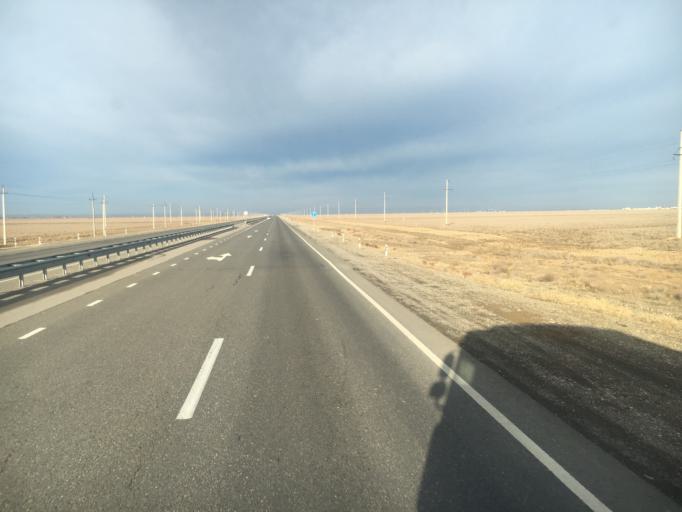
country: KZ
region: Ongtustik Qazaqstan
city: Turkestan
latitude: 43.4291
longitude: 67.9945
